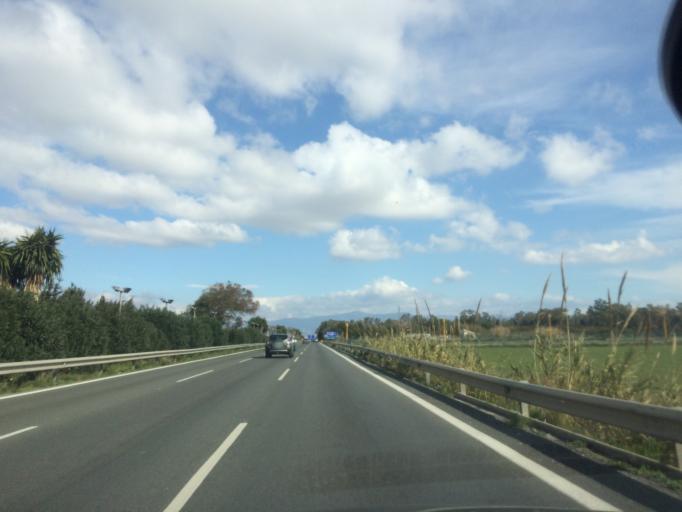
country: ES
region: Andalusia
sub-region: Provincia de Malaga
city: Torremolinos
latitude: 36.6617
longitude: -4.4843
